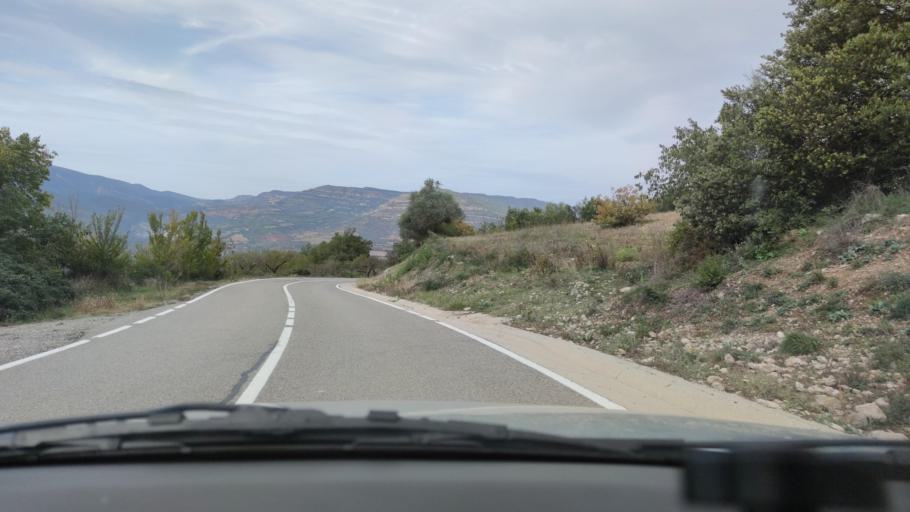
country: ES
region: Catalonia
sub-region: Provincia de Lleida
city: Llimiana
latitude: 42.0684
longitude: 0.9173
